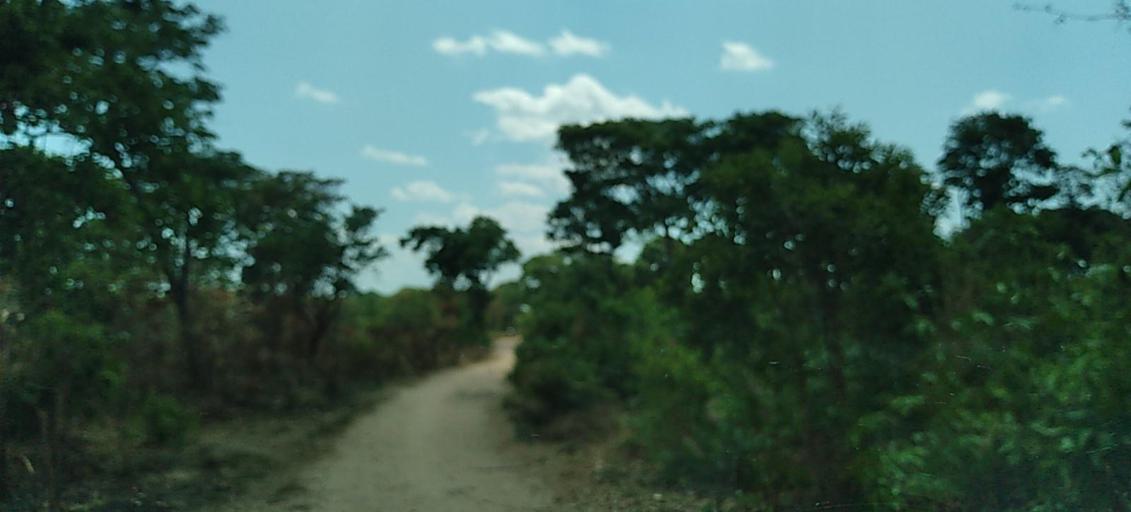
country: ZM
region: Central
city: Kapiri Mposhi
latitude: -13.6334
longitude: 28.7561
